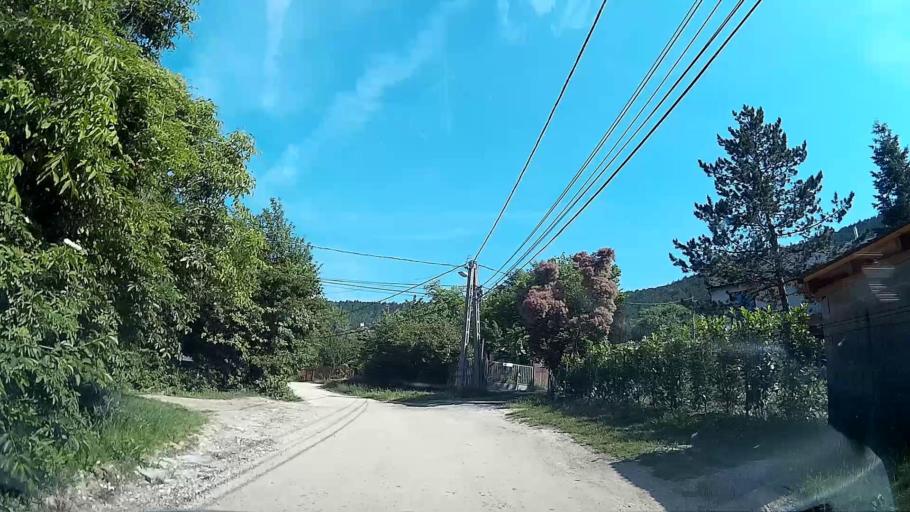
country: HU
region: Pest
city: Pilisborosjeno
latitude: 47.6133
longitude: 18.9938
